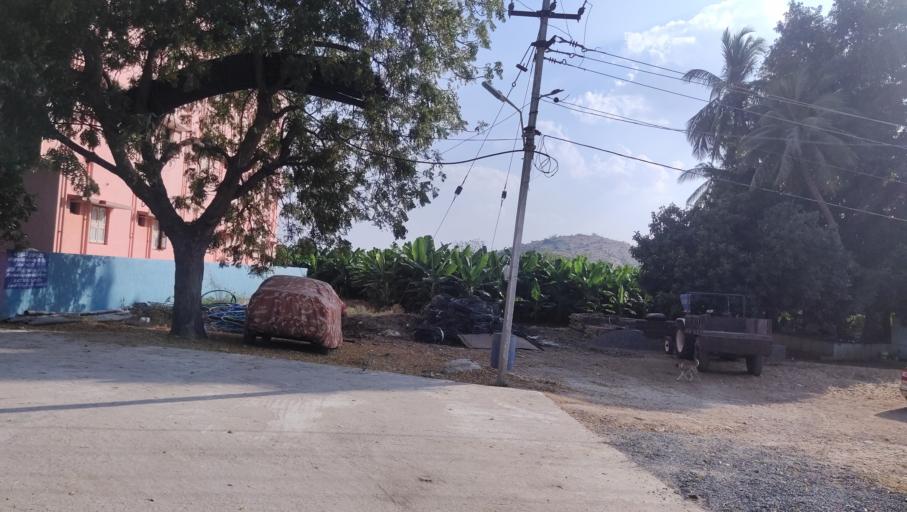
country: IN
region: Andhra Pradesh
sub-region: Anantapur
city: Tadpatri
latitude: 14.9318
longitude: 77.8660
